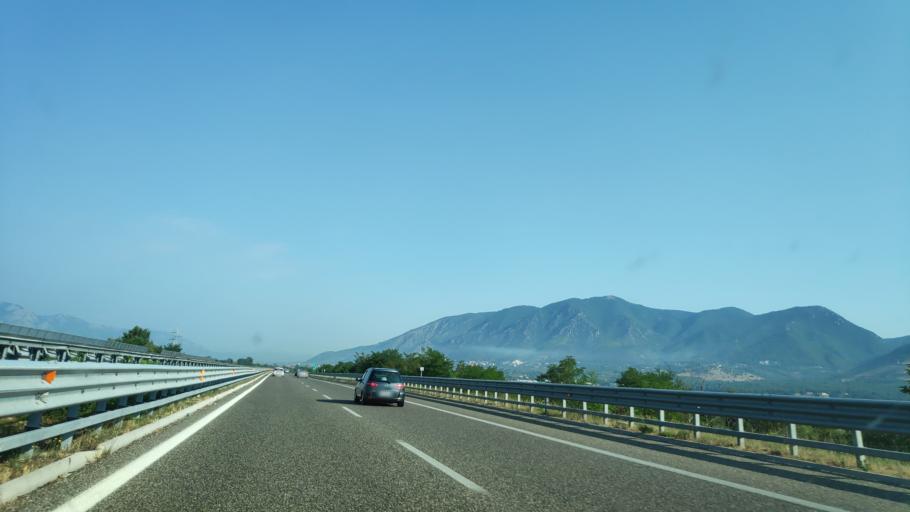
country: IT
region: Campania
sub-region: Provincia di Salerno
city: Padula
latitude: 40.3458
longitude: 15.6210
